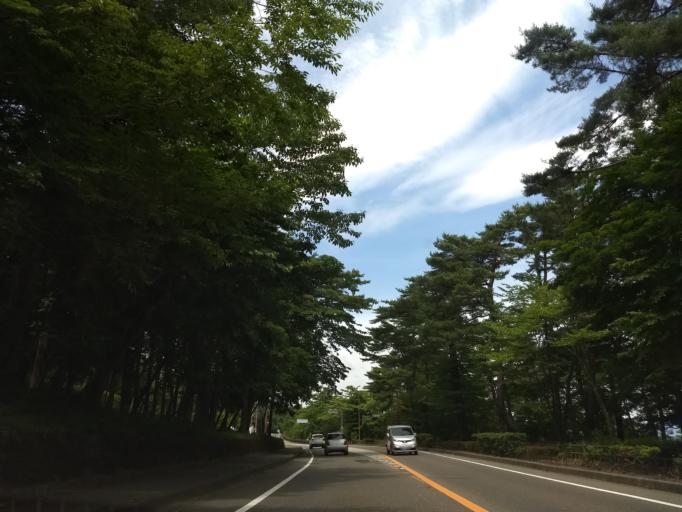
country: JP
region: Shizuoka
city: Gotemba
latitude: 35.4076
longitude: 138.8717
